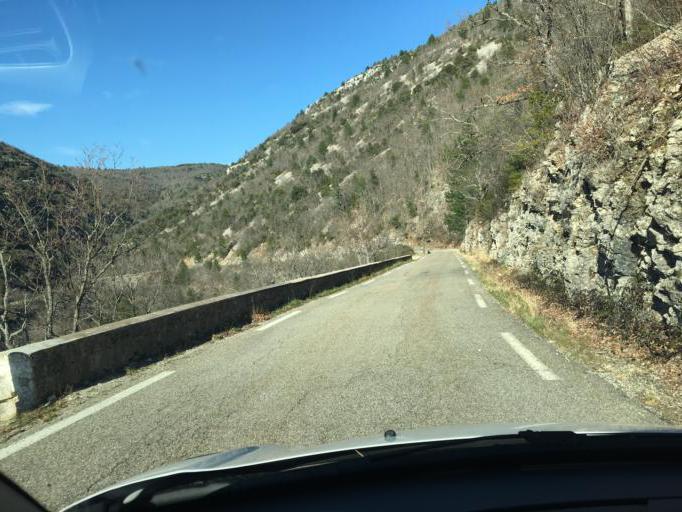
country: FR
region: Provence-Alpes-Cote d'Azur
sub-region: Departement du Vaucluse
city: Villes-sur-Auzon
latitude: 44.0640
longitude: 5.3225
